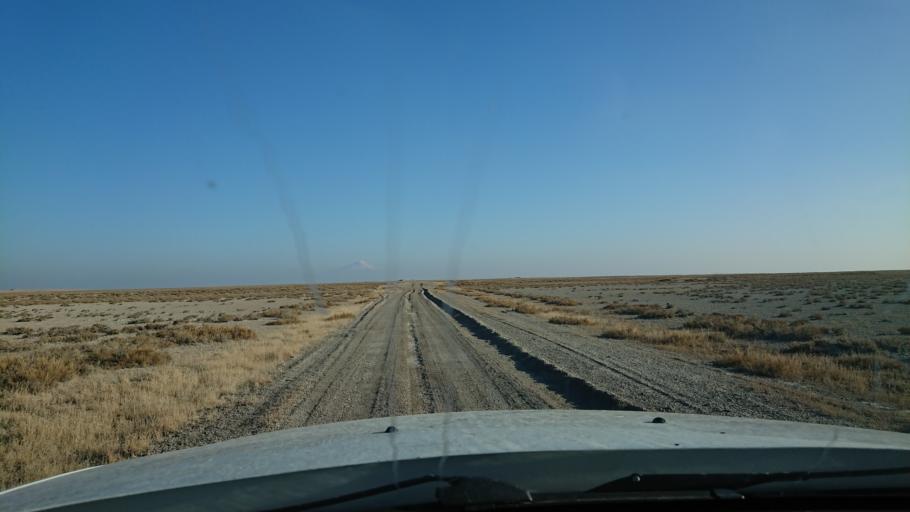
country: TR
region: Aksaray
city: Sultanhani
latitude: 38.4024
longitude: 33.5782
